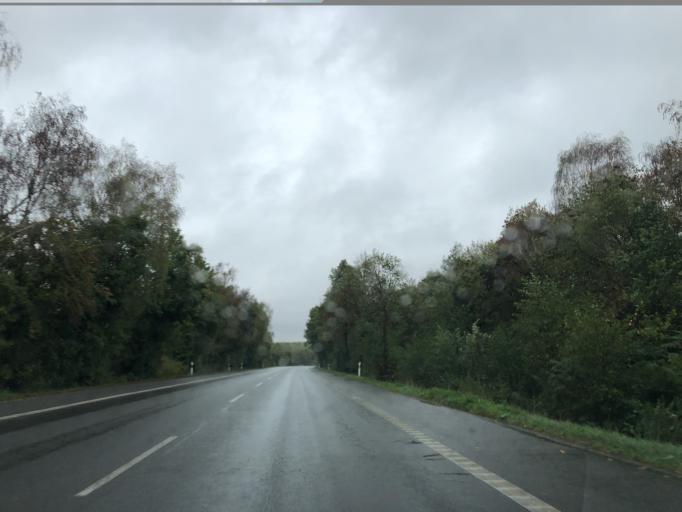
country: DE
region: North Rhine-Westphalia
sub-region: Regierungsbezirk Koln
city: Bedburg
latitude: 51.0296
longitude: 6.5756
